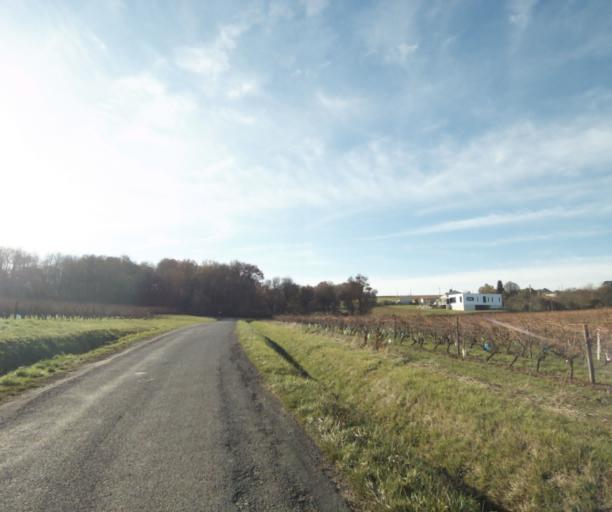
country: FR
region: Poitou-Charentes
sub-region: Departement de la Charente-Maritime
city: Burie
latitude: 45.7683
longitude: -0.4198
